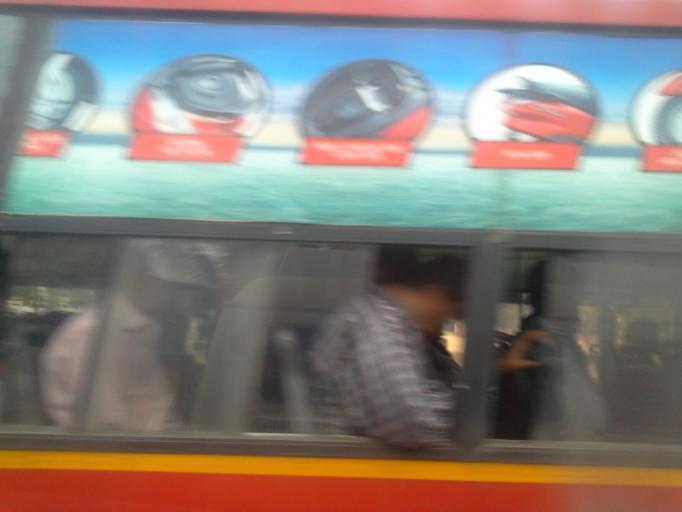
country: IN
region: Karnataka
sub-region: Bangalore Urban
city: Bangalore
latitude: 12.9779
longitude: 77.6061
